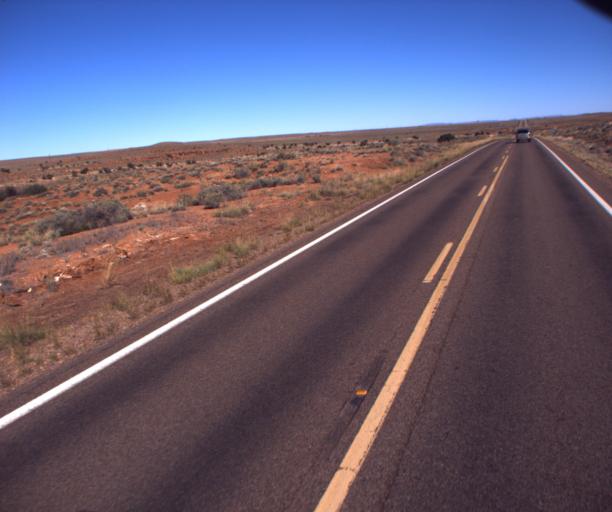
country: US
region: Arizona
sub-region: Navajo County
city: Holbrook
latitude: 34.7667
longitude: -110.1263
